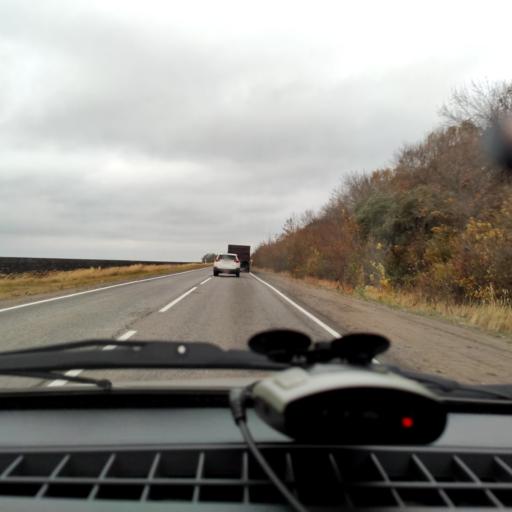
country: RU
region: Voronezj
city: Shilovo
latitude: 51.3856
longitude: 39.0074
